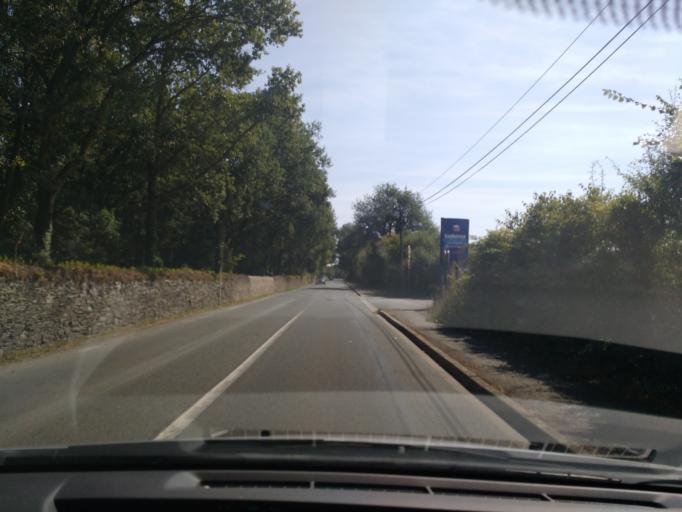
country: FR
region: Pays de la Loire
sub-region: Departement de Maine-et-Loire
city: Trelaze
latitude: 47.4670
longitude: -0.4810
